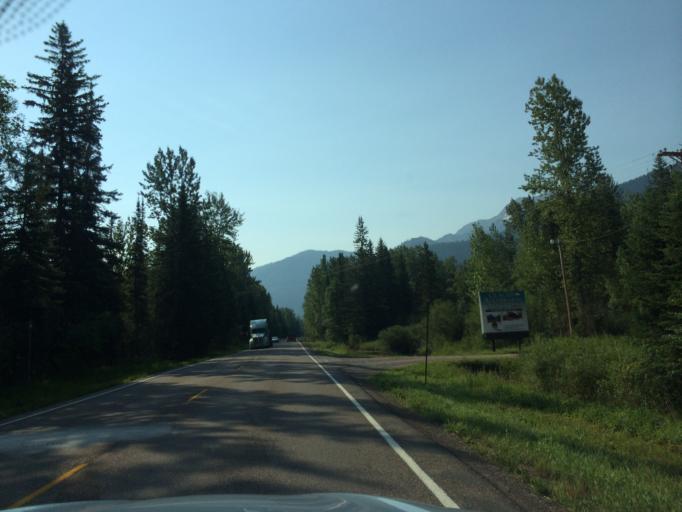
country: US
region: Montana
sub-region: Flathead County
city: Columbia Falls
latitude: 48.4518
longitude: -113.8188
